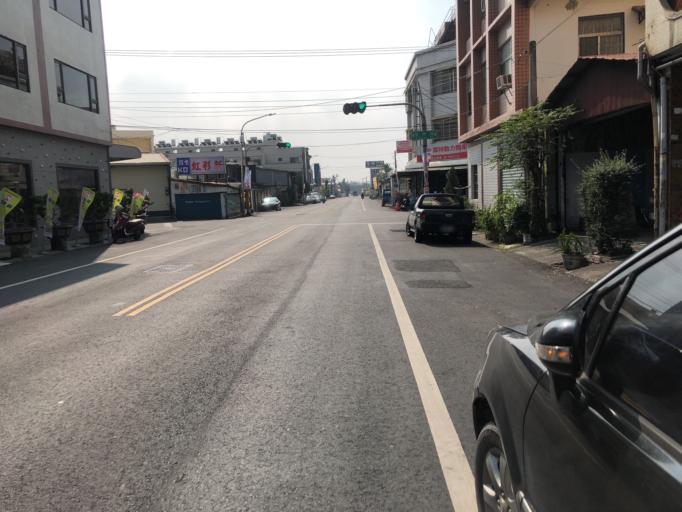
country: TW
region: Taiwan
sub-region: Pingtung
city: Pingtung
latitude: 22.5522
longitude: 120.5343
